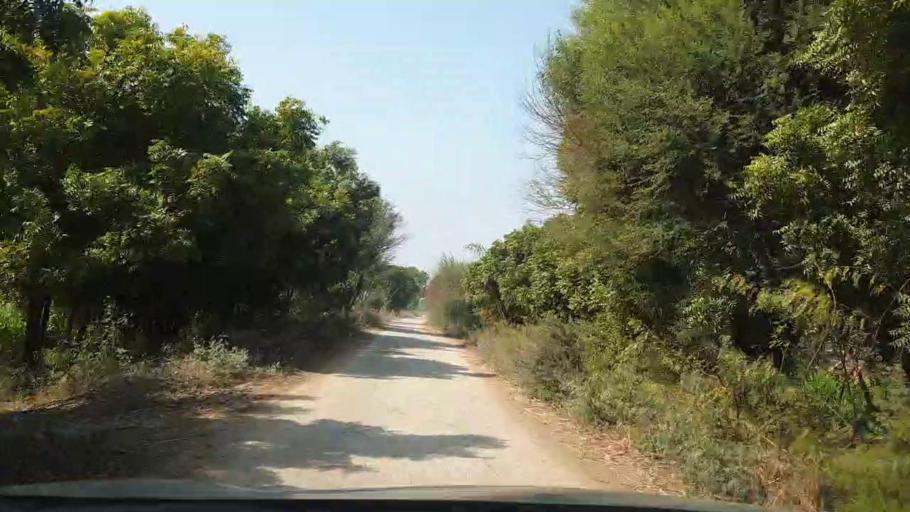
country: PK
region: Sindh
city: Tando Allahyar
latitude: 25.5310
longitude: 68.7777
